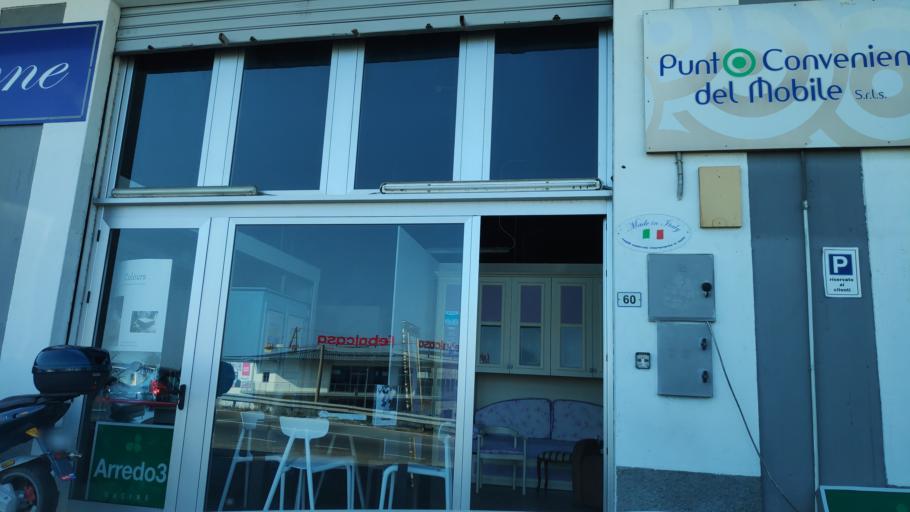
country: IT
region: Calabria
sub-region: Provincia di Catanzaro
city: Martelli-Laganosa
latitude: 38.6796
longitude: 16.5386
